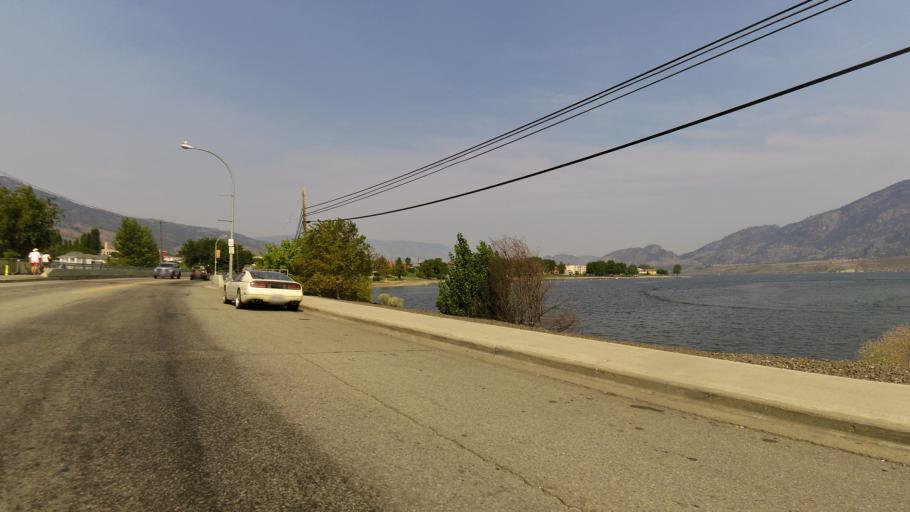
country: CA
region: British Columbia
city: Osoyoos
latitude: 49.0282
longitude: -119.4587
